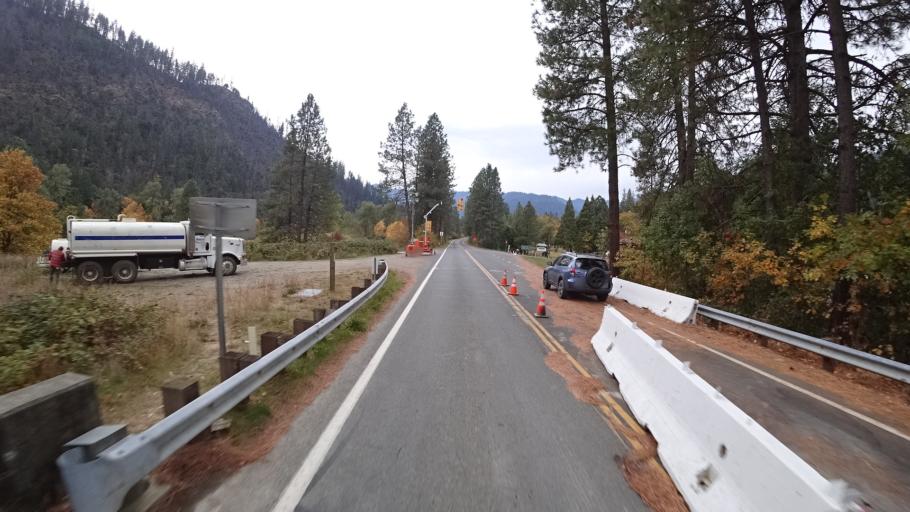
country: US
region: California
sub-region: Siskiyou County
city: Happy Camp
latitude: 41.7907
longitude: -123.3796
